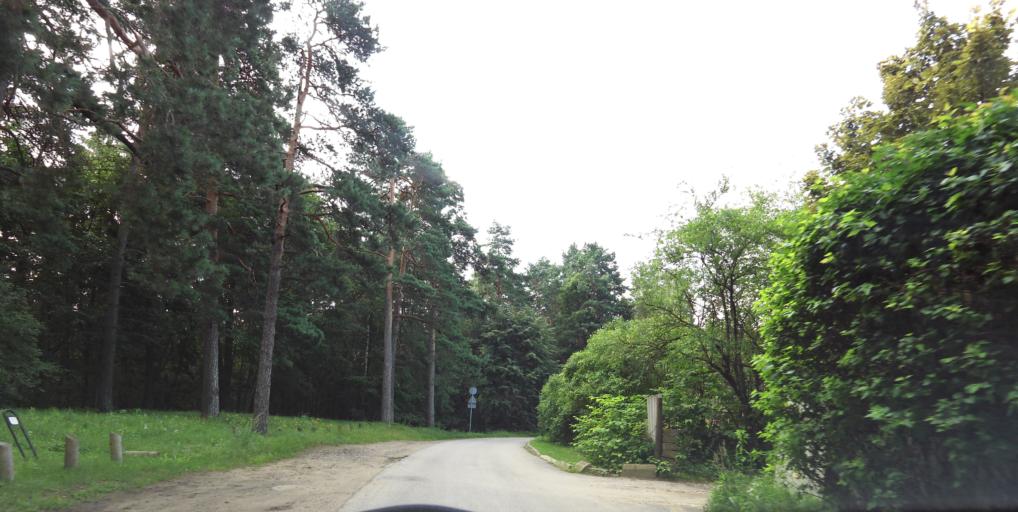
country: LT
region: Vilnius County
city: Seskine
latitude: 54.7335
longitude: 25.2844
